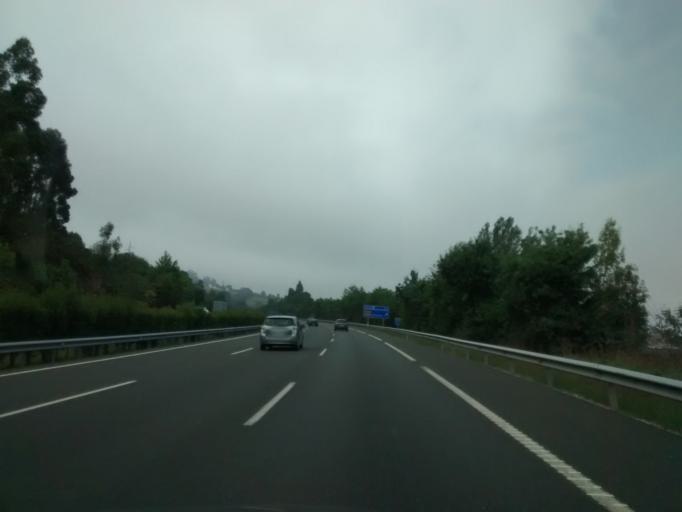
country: ES
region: Cantabria
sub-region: Provincia de Cantabria
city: Reocin
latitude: 43.3478
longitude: -4.1201
